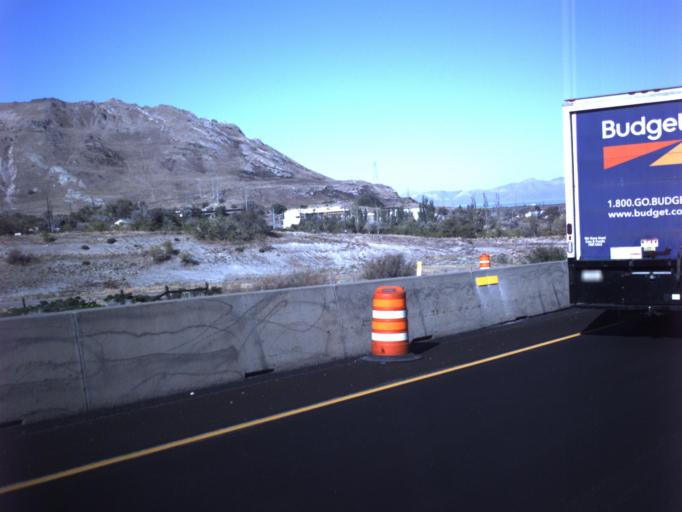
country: US
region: Utah
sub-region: Salt Lake County
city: Magna
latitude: 40.7232
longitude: -112.1586
